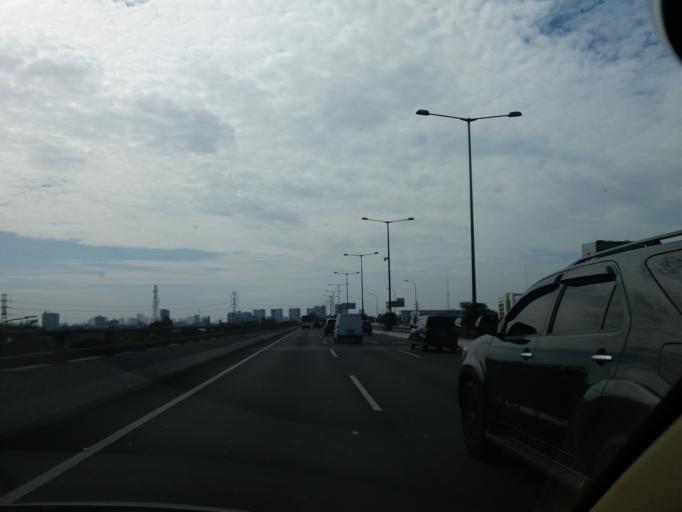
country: ID
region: Jakarta Raya
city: Jakarta
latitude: -6.2108
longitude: 106.8739
